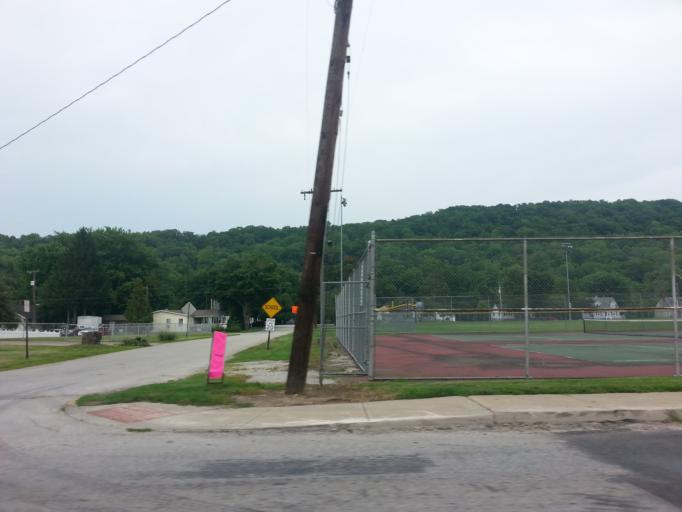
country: US
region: Ohio
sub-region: Brown County
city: Ripley
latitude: 38.7389
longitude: -83.8413
